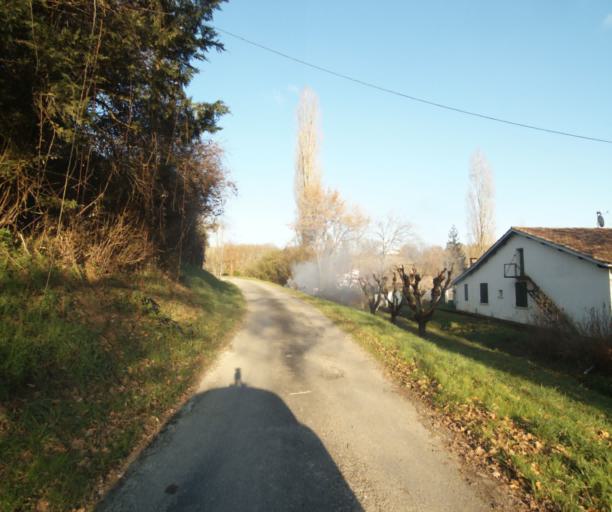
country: FR
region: Midi-Pyrenees
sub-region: Departement du Tarn-et-Garonne
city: Moissac
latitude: 44.1294
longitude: 1.1301
